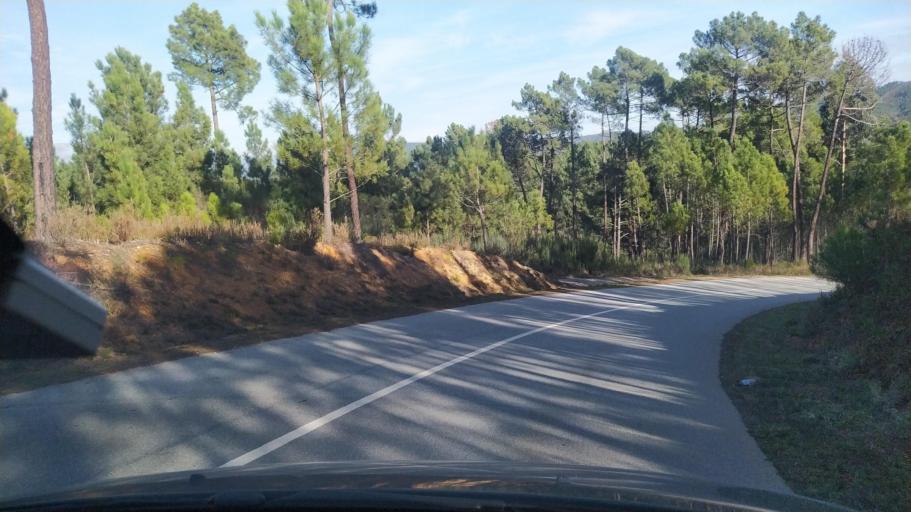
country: PT
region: Castelo Branco
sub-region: Concelho do Fundao
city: Aldeia de Joanes
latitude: 40.1807
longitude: -7.6608
